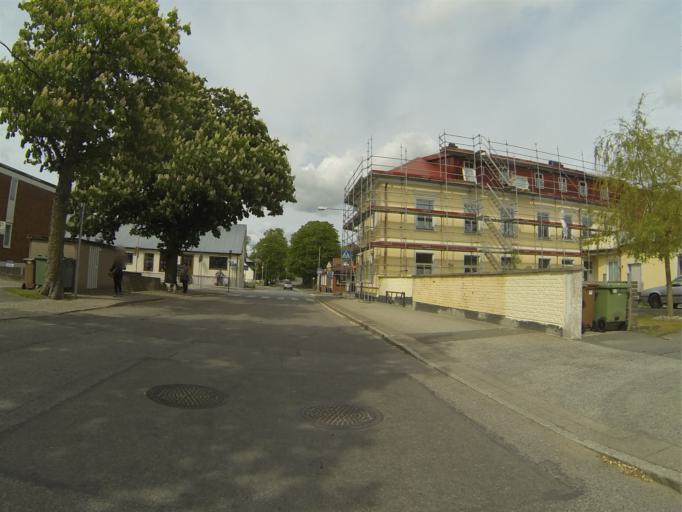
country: SE
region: Skane
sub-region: Tomelilla Kommun
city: Tomelilla
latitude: 55.5435
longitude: 13.9550
